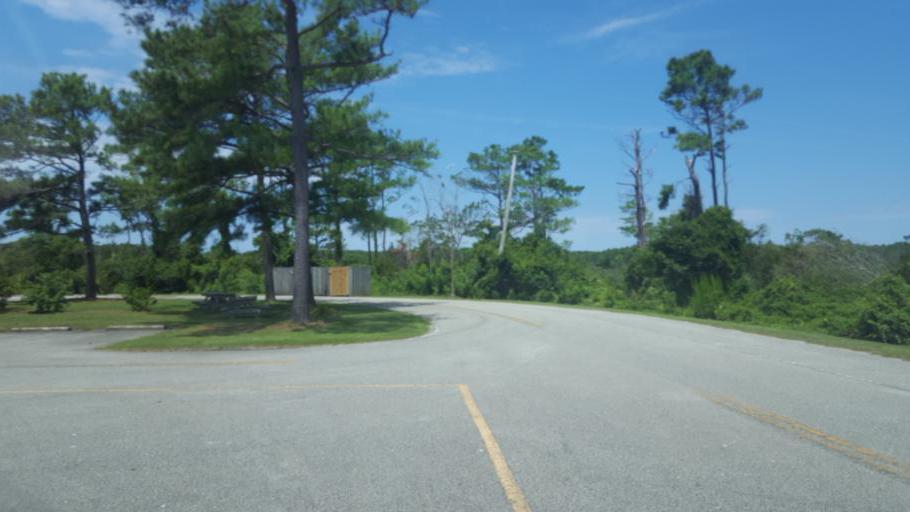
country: US
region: North Carolina
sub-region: Dare County
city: Manteo
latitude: 35.9119
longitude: -75.6647
